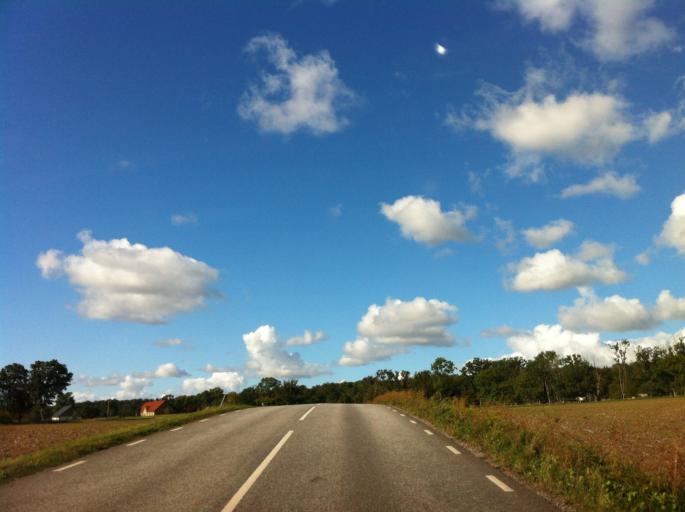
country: SE
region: Skane
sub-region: Sjobo Kommun
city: Blentarp
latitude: 55.6973
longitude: 13.6012
